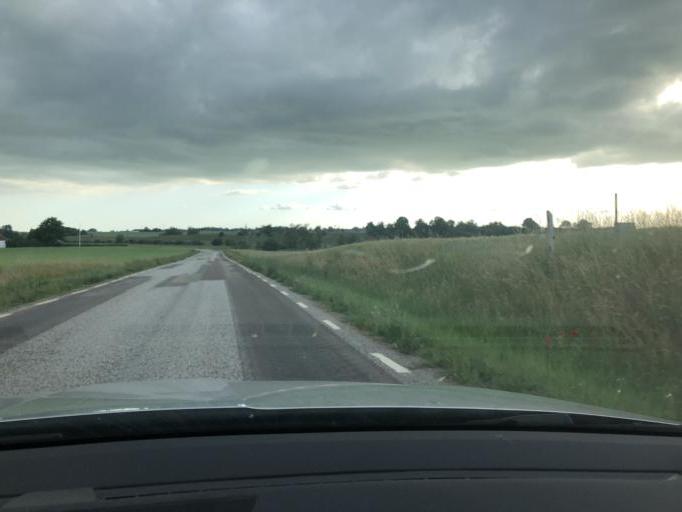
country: SE
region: Skane
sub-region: Simrishamns Kommun
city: Simrishamn
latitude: 55.5086
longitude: 14.2289
